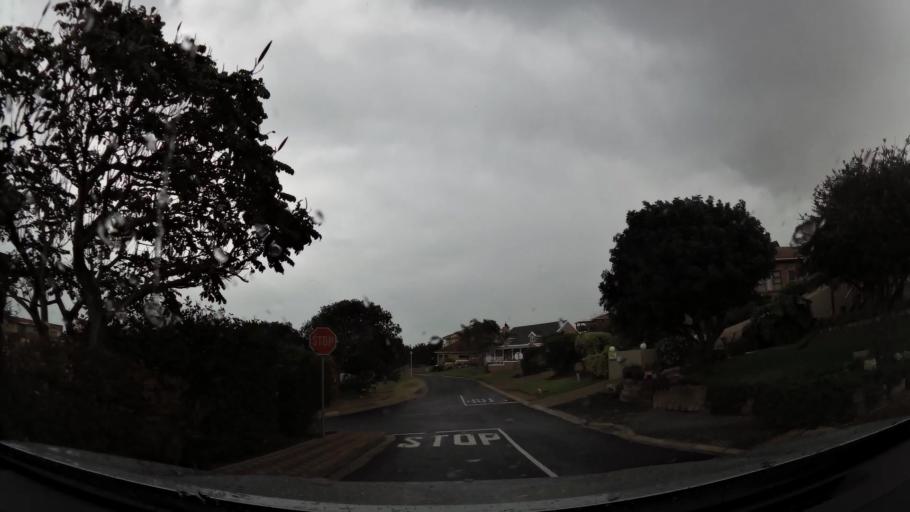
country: ZA
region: Western Cape
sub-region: Eden District Municipality
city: George
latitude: -34.0477
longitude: 22.2894
